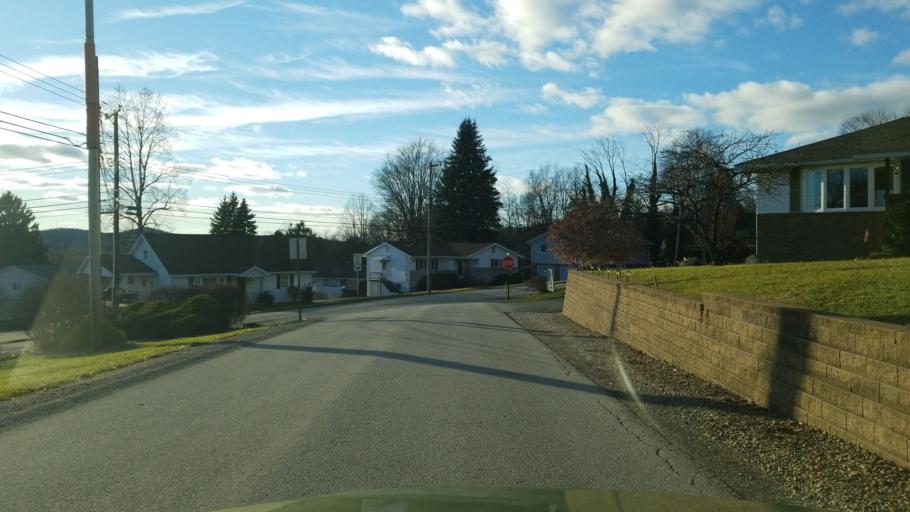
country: US
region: Pennsylvania
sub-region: Indiana County
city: Indiana
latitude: 40.6248
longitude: -79.1784
